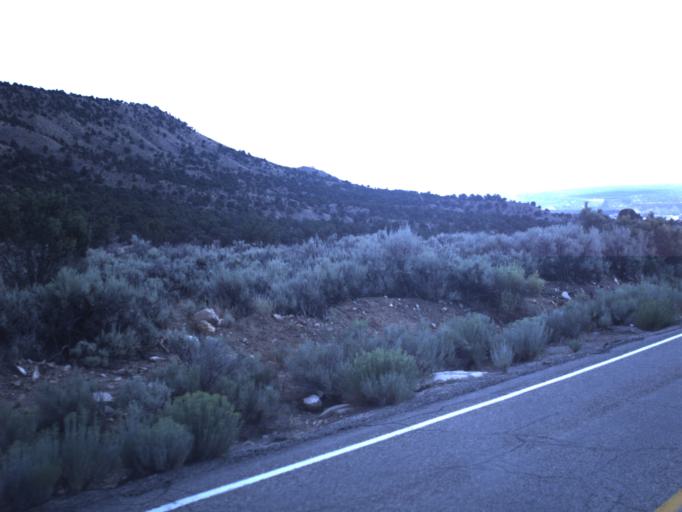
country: US
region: Utah
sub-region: Carbon County
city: Spring Glen
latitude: 39.6725
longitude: -110.8283
